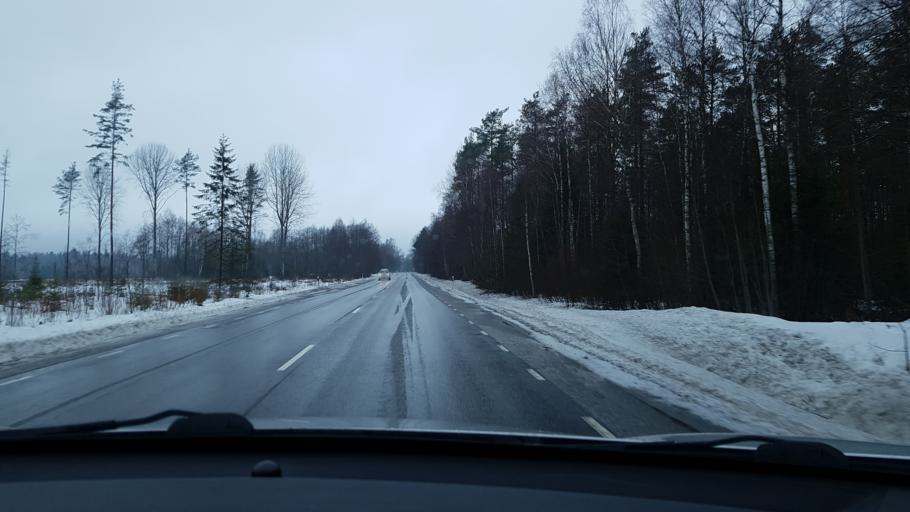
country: EE
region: Paernumaa
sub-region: Vaendra vald (alev)
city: Vandra
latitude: 58.8187
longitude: 25.1559
